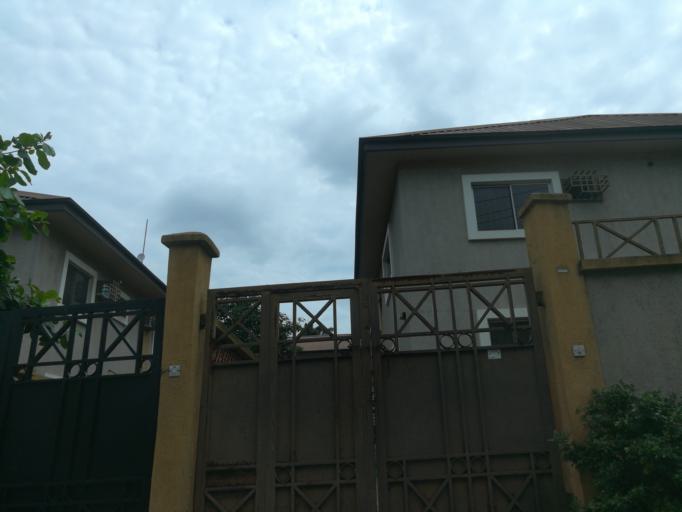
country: NG
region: Lagos
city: Ojota
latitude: 6.5771
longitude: 3.3693
